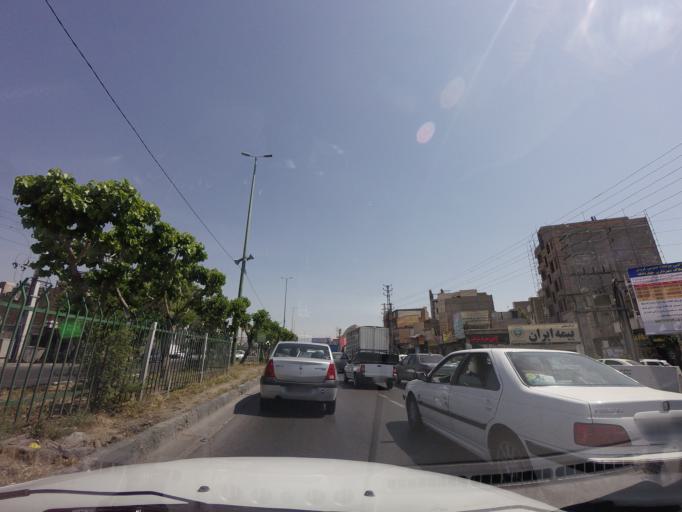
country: IR
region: Tehran
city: Eslamshahr
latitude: 35.6071
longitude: 51.3063
